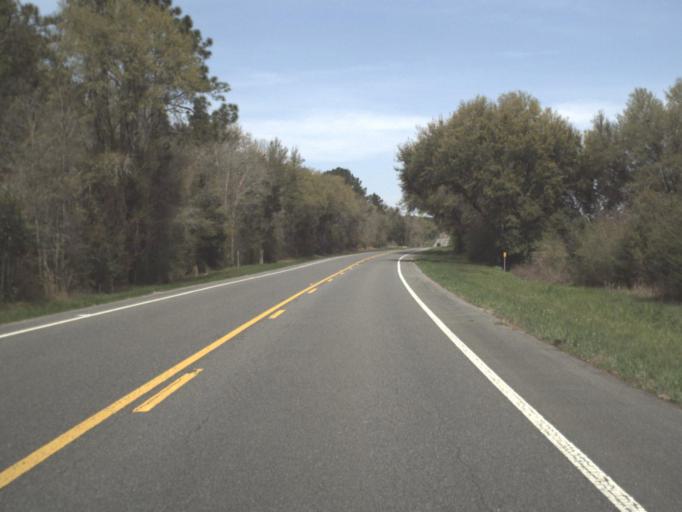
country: US
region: Florida
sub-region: Walton County
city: DeFuniak Springs
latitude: 30.8212
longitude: -85.9578
